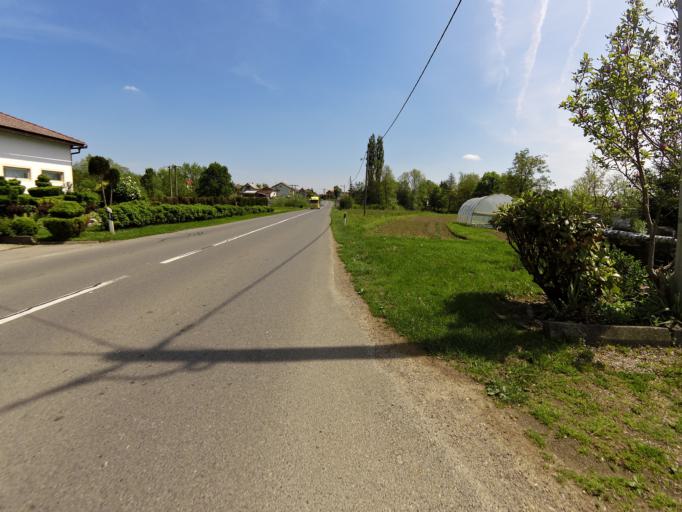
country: HR
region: Karlovacka
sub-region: Grad Karlovac
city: Karlovac
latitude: 45.5579
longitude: 15.5239
